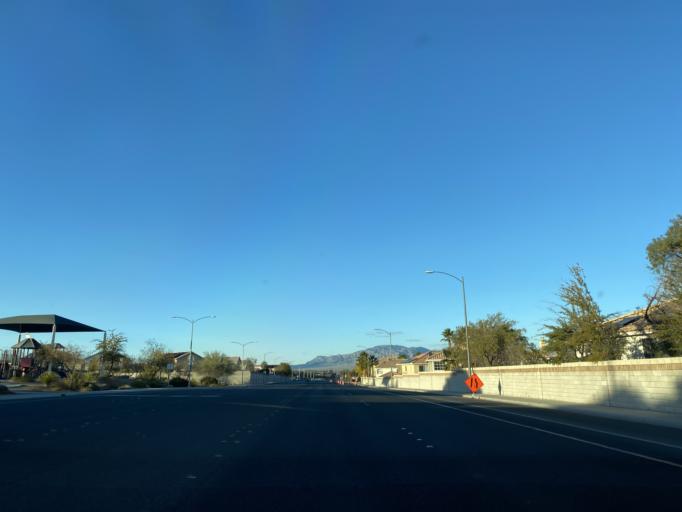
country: US
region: Nevada
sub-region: Clark County
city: Summerlin South
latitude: 36.2305
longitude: -115.2975
